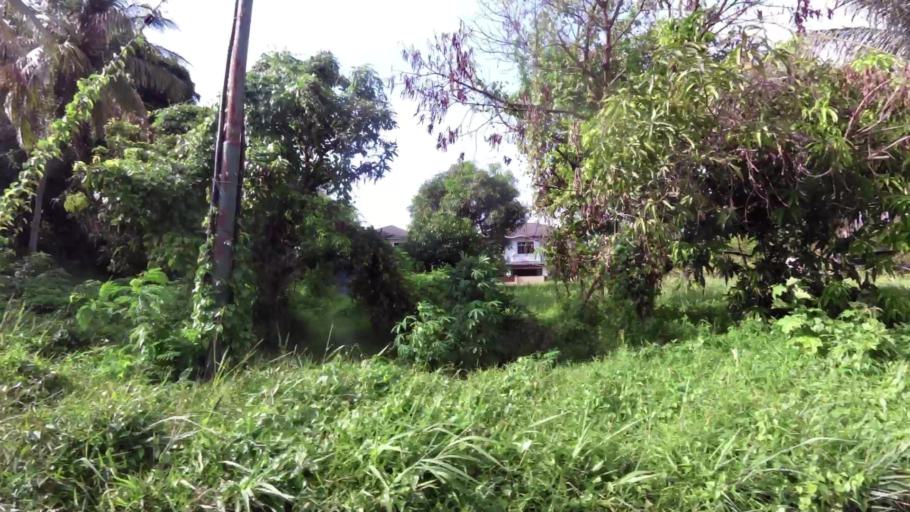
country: BN
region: Brunei and Muara
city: Bandar Seri Begawan
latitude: 4.9589
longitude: 114.9628
